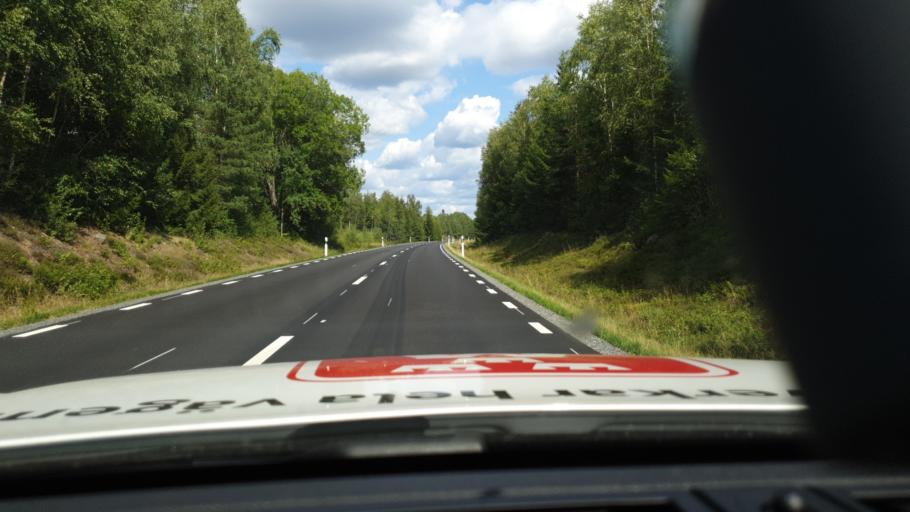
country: SE
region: Joenkoeping
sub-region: Vaggeryds Kommun
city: Skillingaryd
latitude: 57.4092
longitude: 14.0672
